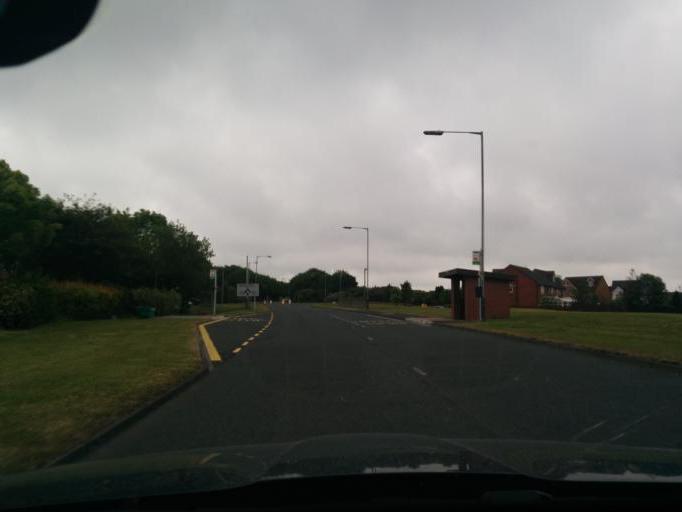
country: GB
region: England
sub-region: Northumberland
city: Cramlington
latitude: 55.0966
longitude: -1.5837
